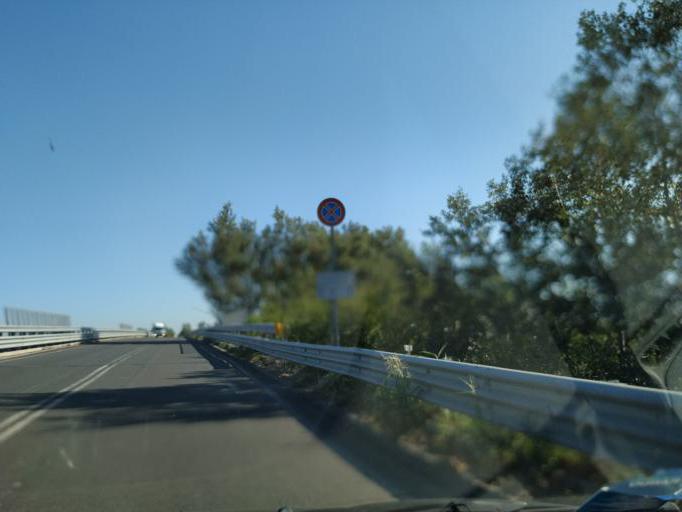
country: IT
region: Emilia-Romagna
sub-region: Provincia di Bologna
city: San Giovanni in Persiceto
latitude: 44.6541
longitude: 11.1792
